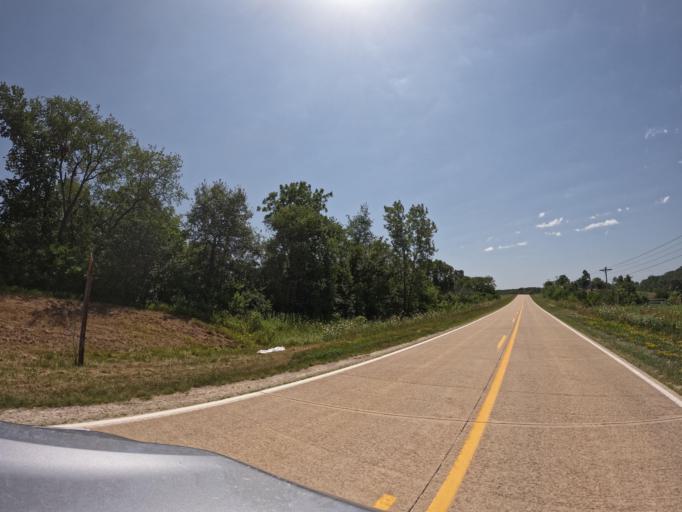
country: US
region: Iowa
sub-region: Henry County
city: Mount Pleasant
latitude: 40.9231
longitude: -91.5541
